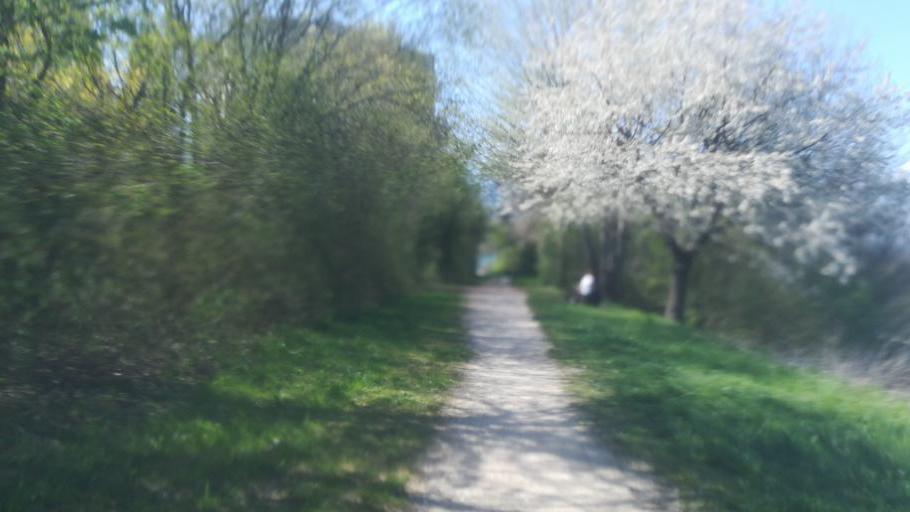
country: DE
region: Baden-Wuerttemberg
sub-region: Freiburg Region
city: Singen
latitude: 47.7788
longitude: 8.8578
